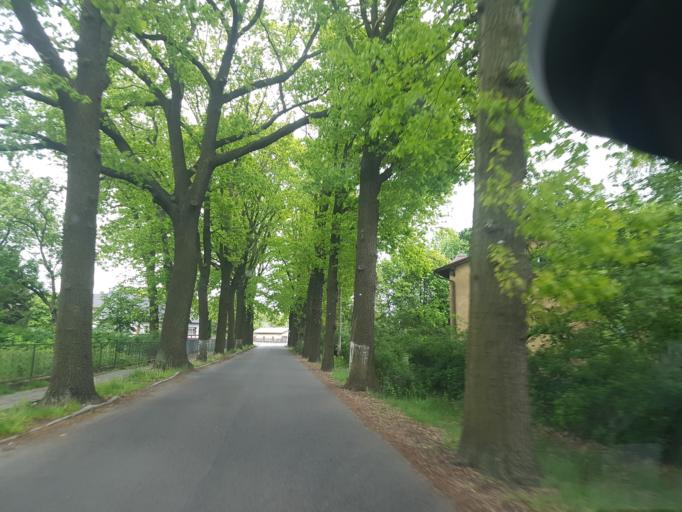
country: DE
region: Brandenburg
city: Neupetershain
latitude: 51.6077
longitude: 14.1607
